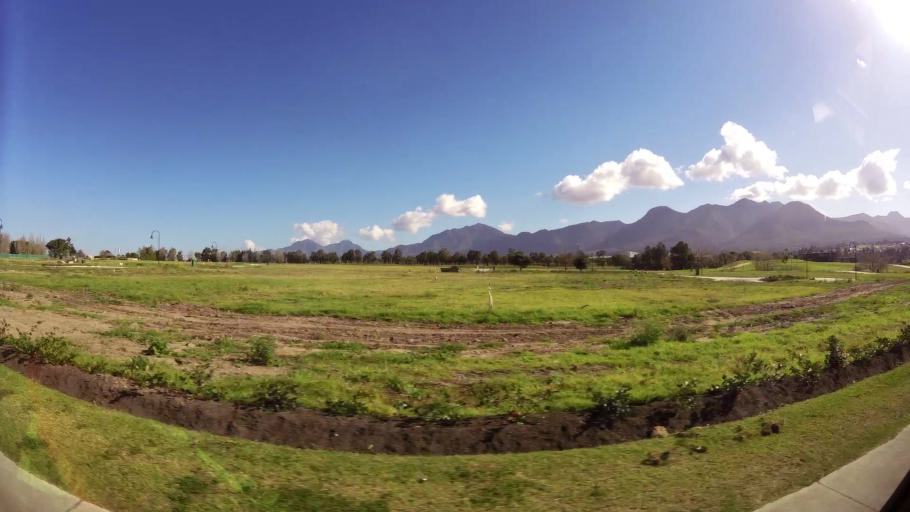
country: ZA
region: Western Cape
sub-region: Eden District Municipality
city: George
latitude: -33.9617
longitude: 22.4026
